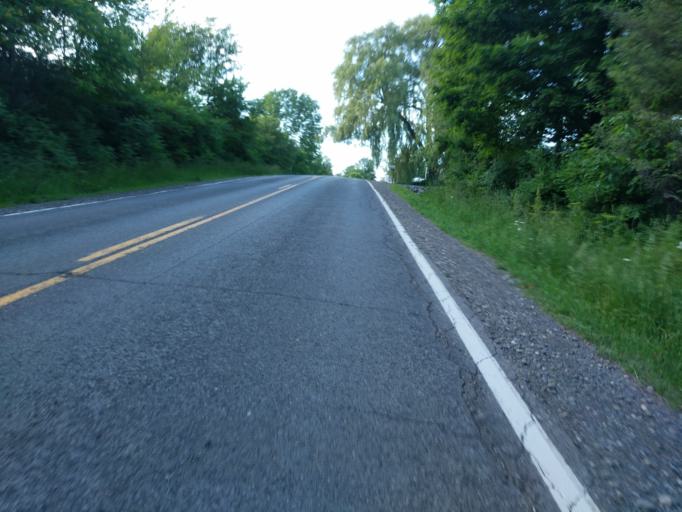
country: US
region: New York
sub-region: Tompkins County
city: Dryden
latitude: 42.3966
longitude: -76.3507
